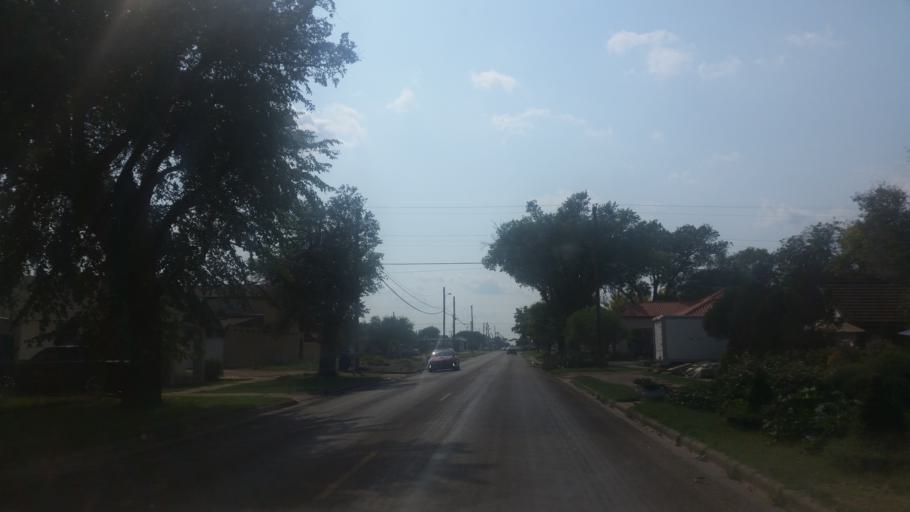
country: US
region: New Mexico
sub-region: Curry County
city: Clovis
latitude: 34.4120
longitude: -103.2017
